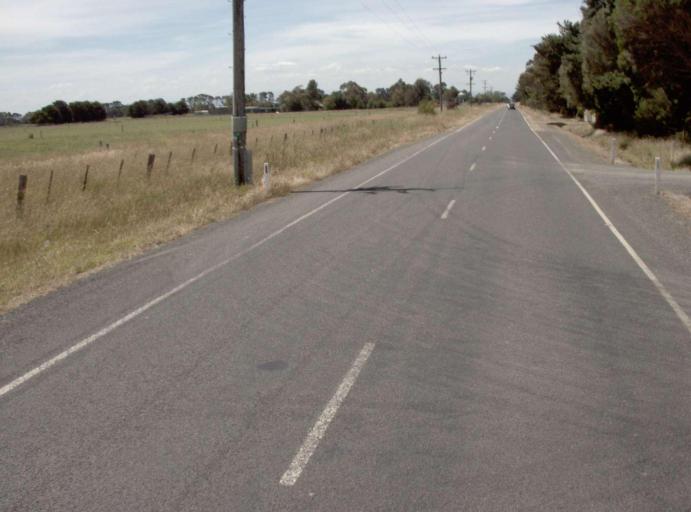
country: AU
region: Victoria
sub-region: Wellington
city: Heyfield
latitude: -38.0803
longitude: 146.8686
